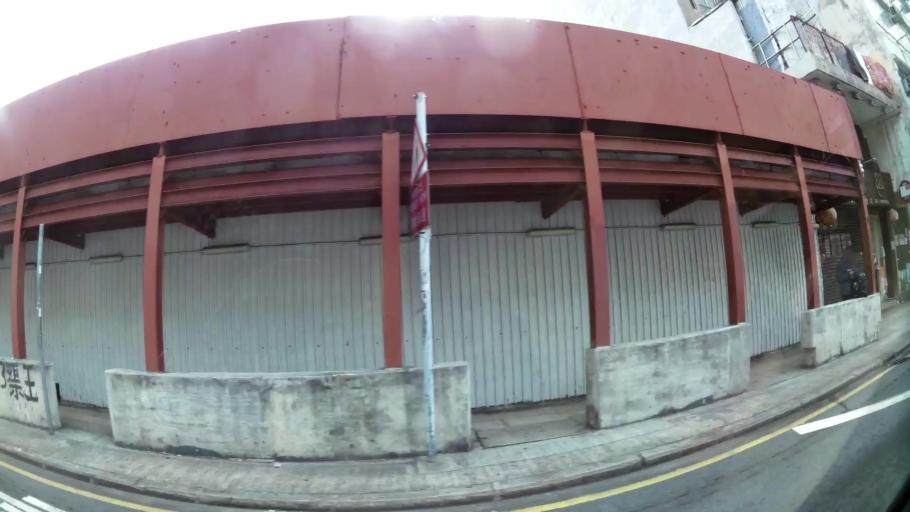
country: HK
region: Kowloon City
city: Kowloon
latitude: 22.3302
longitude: 114.1871
